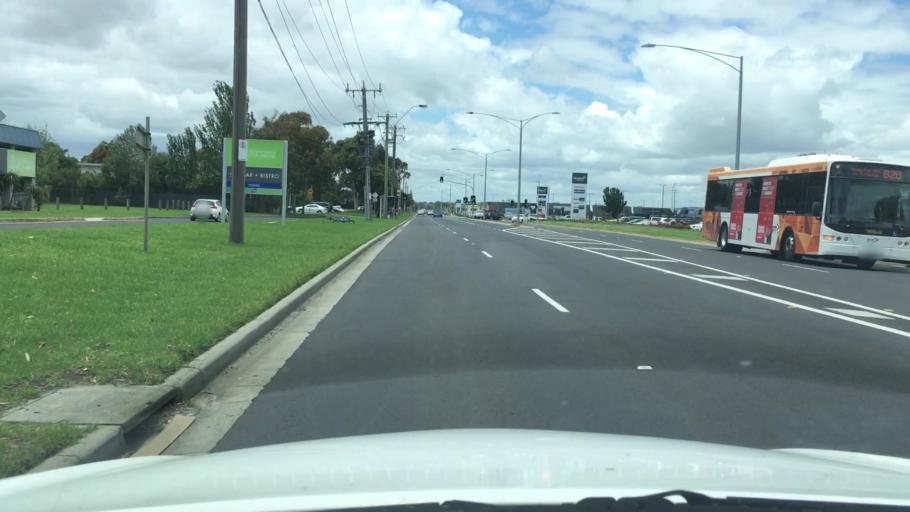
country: AU
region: Victoria
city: Heatherton
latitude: -37.9694
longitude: 145.0889
